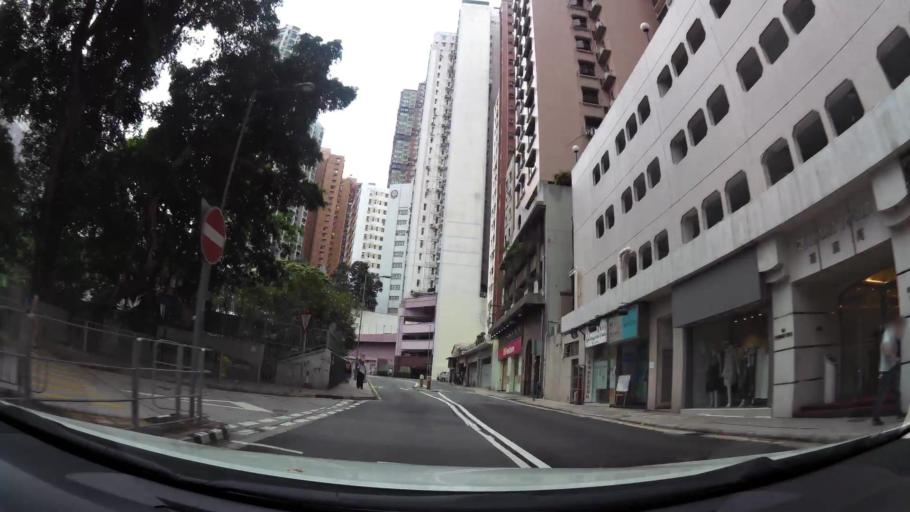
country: HK
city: Hong Kong
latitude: 22.2844
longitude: 114.1432
